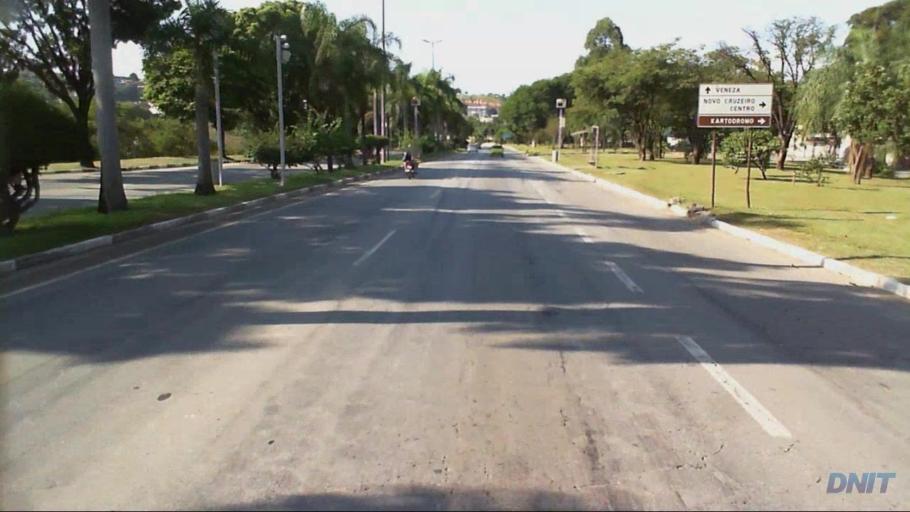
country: BR
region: Minas Gerais
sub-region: Ipatinga
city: Ipatinga
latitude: -19.4718
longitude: -42.5400
